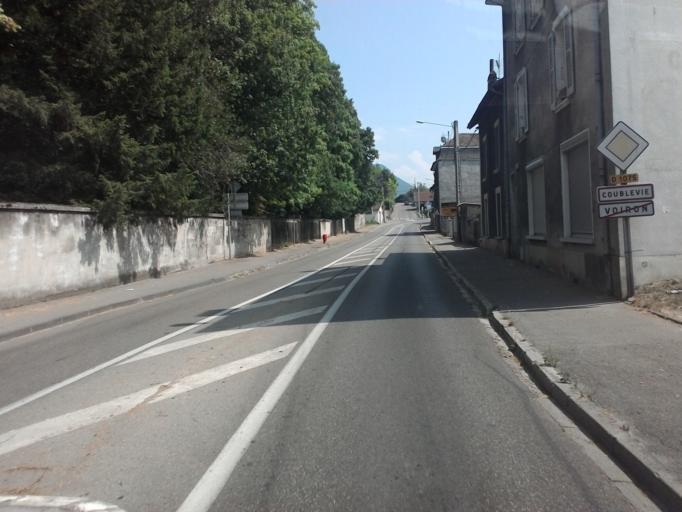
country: FR
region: Rhone-Alpes
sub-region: Departement de l'Isere
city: Voiron
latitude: 45.3596
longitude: 5.6004
